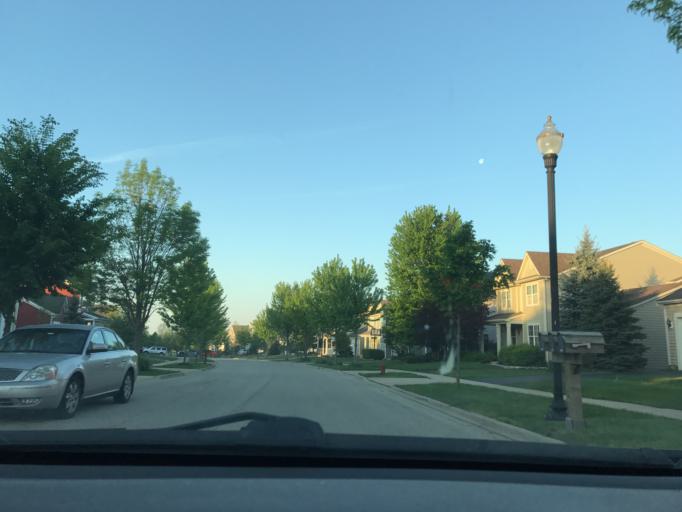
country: US
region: Illinois
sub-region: Kane County
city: Pingree Grove
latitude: 42.0319
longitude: -88.3629
